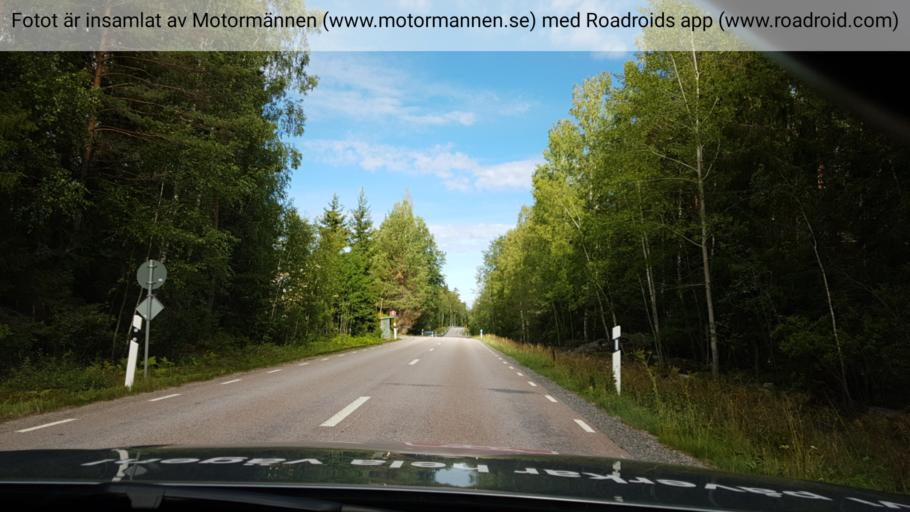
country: SE
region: Uppsala
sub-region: Heby Kommun
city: OEstervala
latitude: 60.0122
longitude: 17.2919
